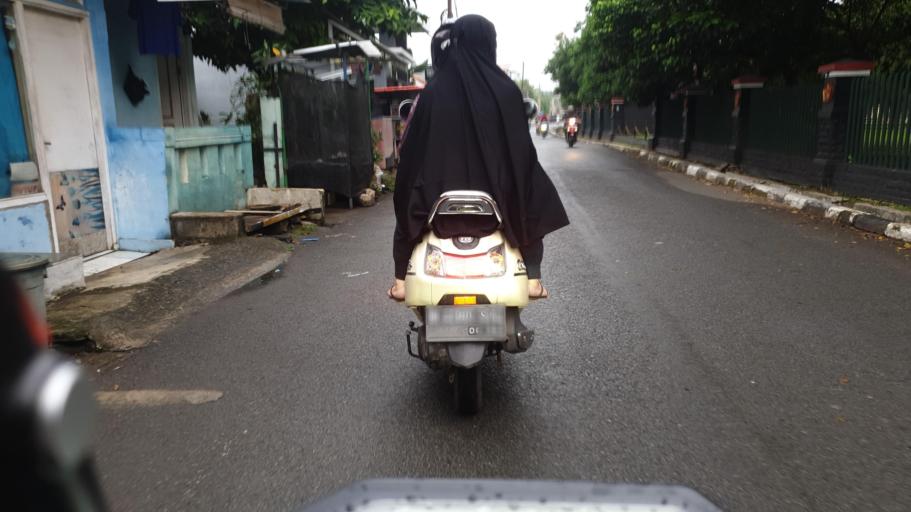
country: ID
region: West Java
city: Depok
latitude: -6.3430
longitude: 106.8302
